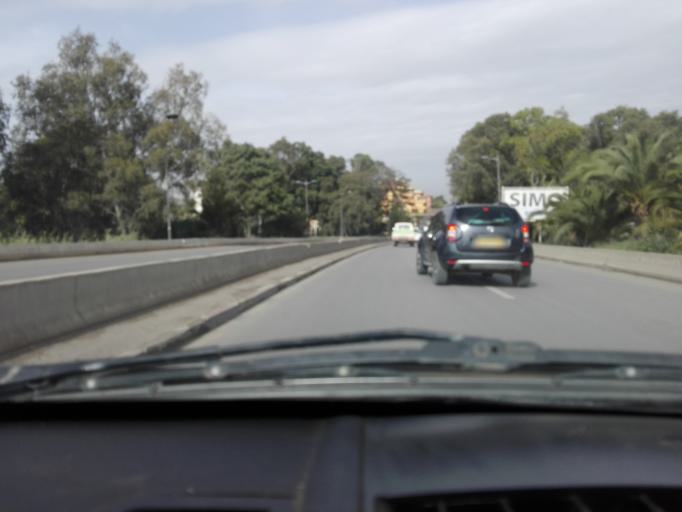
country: DZ
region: Alger
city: Bab Ezzouar
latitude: 36.7253
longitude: 3.1958
